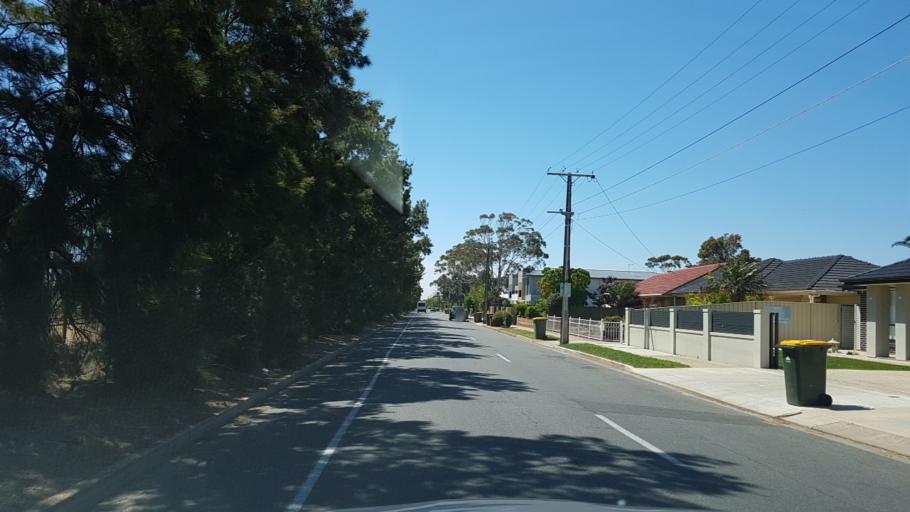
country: AU
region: South Australia
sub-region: Marion
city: Plympton Park
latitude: -34.9804
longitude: 138.5472
